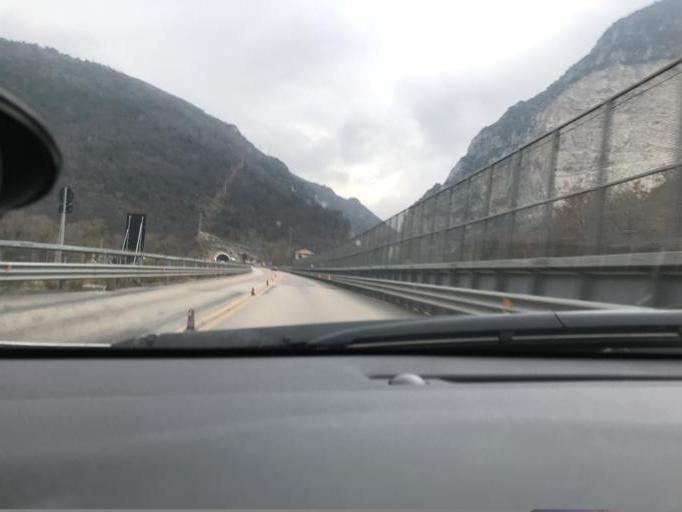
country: IT
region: The Marches
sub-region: Provincia di Ancona
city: Serra San Quirico
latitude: 43.4329
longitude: 13.0153
